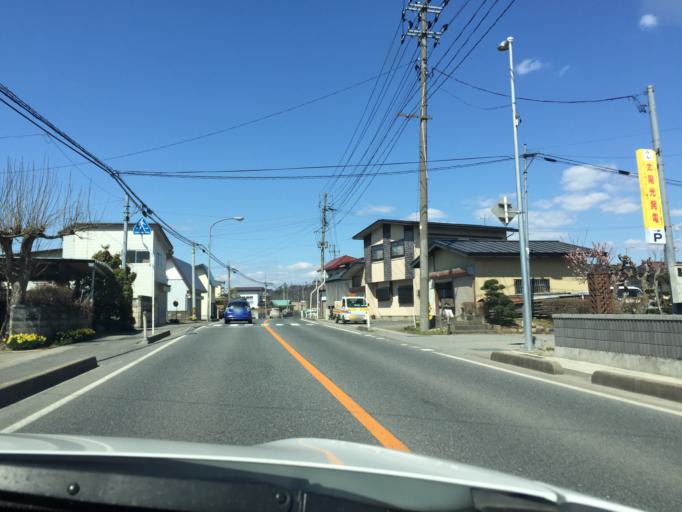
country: JP
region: Yamagata
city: Nagai
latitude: 38.0851
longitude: 140.0410
